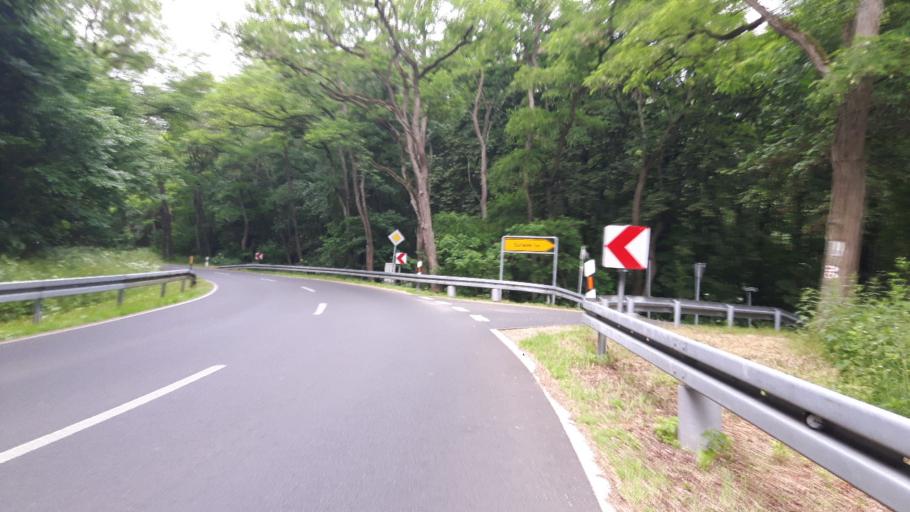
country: DE
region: Brandenburg
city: Mescherin
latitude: 53.2694
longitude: 14.4317
